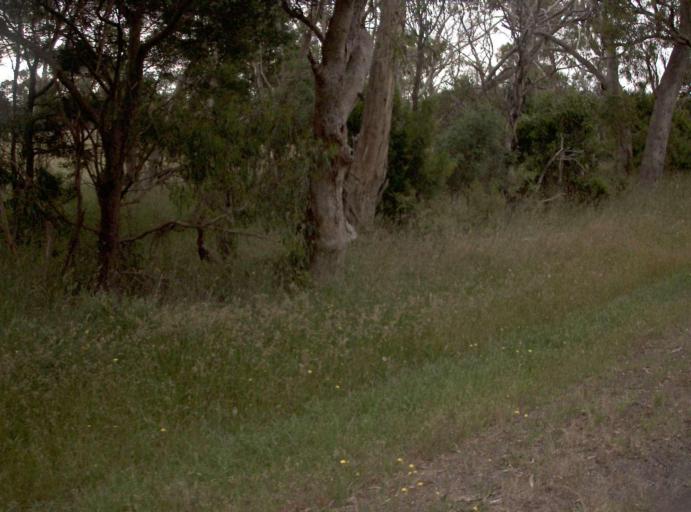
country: AU
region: Victoria
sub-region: Latrobe
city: Traralgon
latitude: -38.5458
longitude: 146.8309
